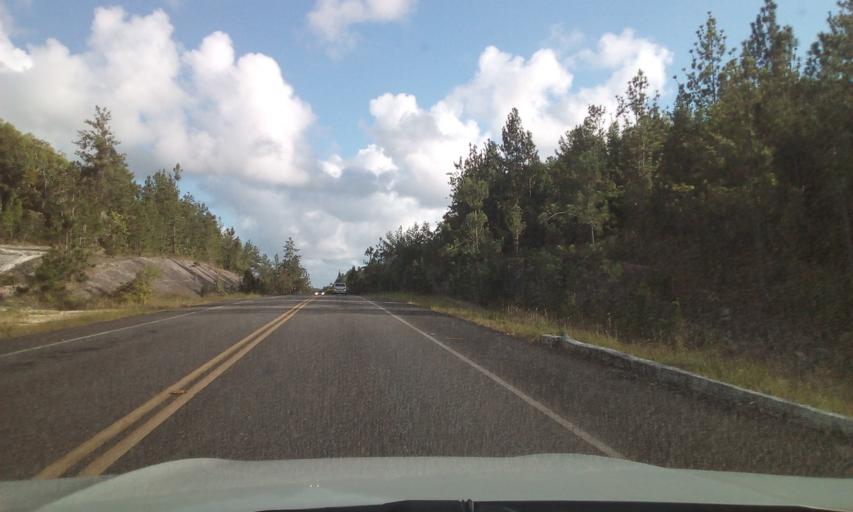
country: BR
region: Bahia
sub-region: Entre Rios
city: Entre Rios
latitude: -12.1220
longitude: -37.7890
